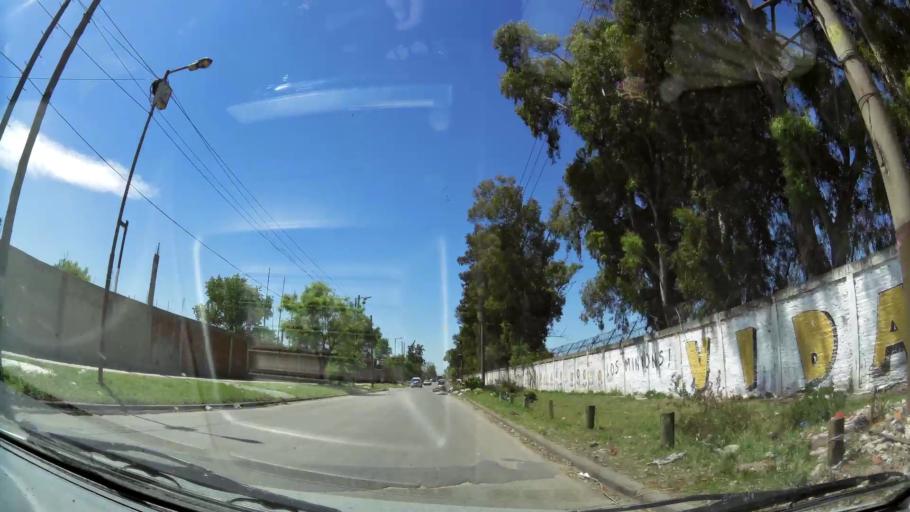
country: AR
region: Buenos Aires
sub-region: Partido de Quilmes
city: Quilmes
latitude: -34.7299
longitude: -58.3209
